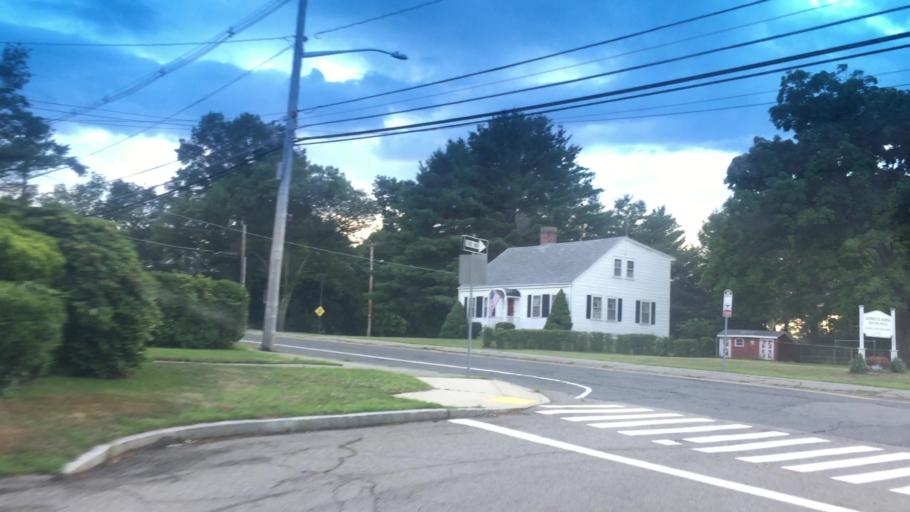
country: US
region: Massachusetts
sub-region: Norfolk County
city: Norwood
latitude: 42.1715
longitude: -71.2093
